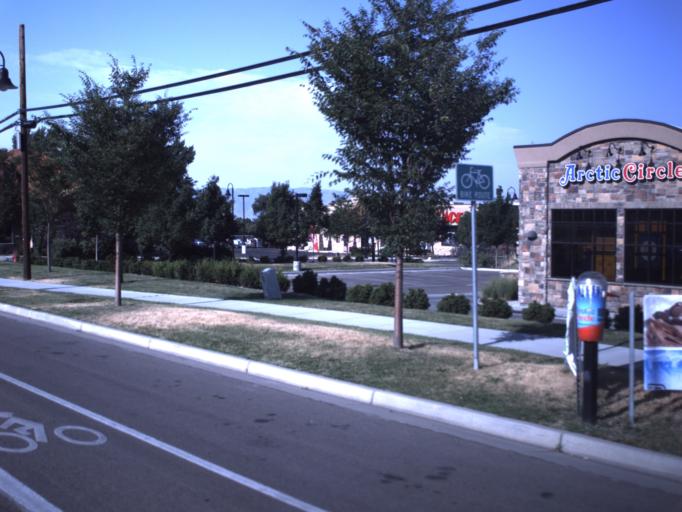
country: US
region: Utah
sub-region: Utah County
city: Alpine
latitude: 40.4296
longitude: -111.7855
